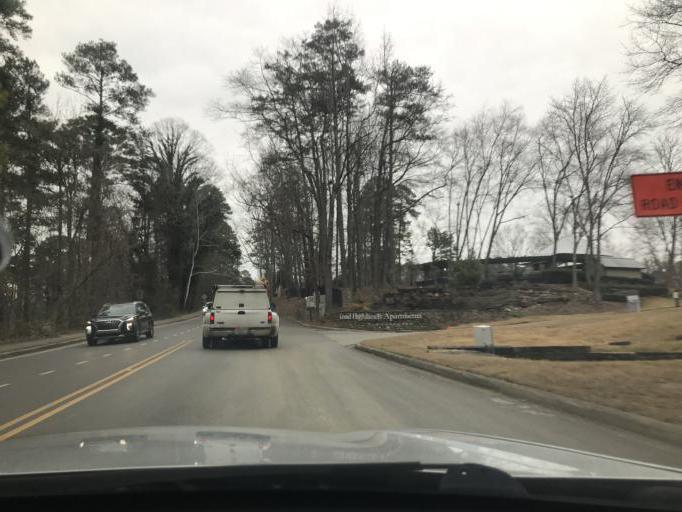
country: US
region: Alabama
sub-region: Jefferson County
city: Cahaba Heights
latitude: 33.4677
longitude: -86.7303
